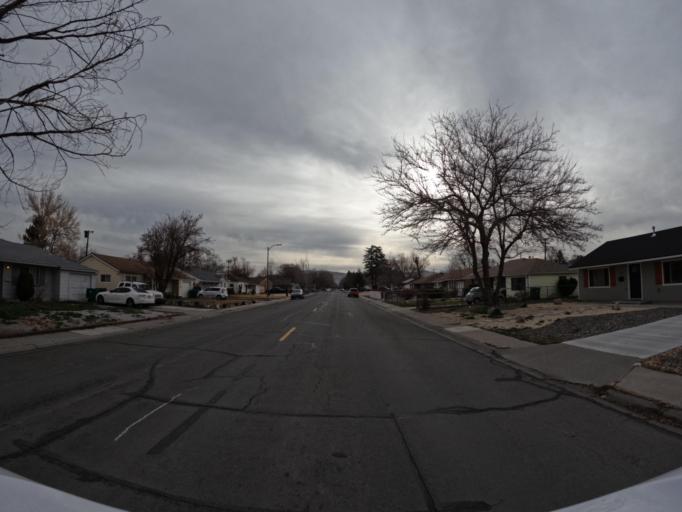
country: US
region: Nevada
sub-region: Washoe County
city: Sparks
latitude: 39.5438
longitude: -119.7496
